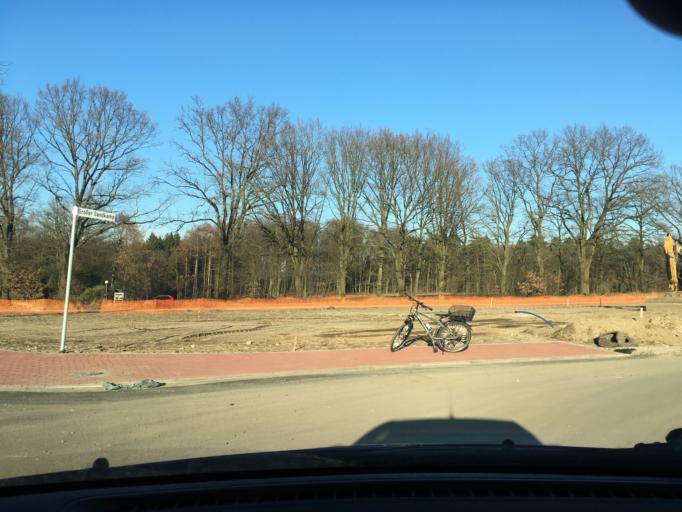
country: DE
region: Schleswig-Holstein
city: Buchen
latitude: 53.4778
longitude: 10.5961
